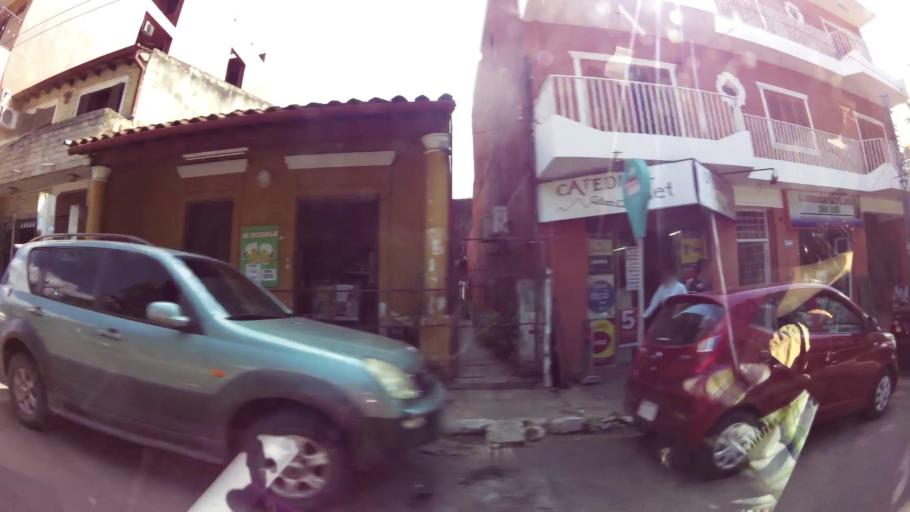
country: PY
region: Central
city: San Lorenzo
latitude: -25.3423
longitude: -57.5089
